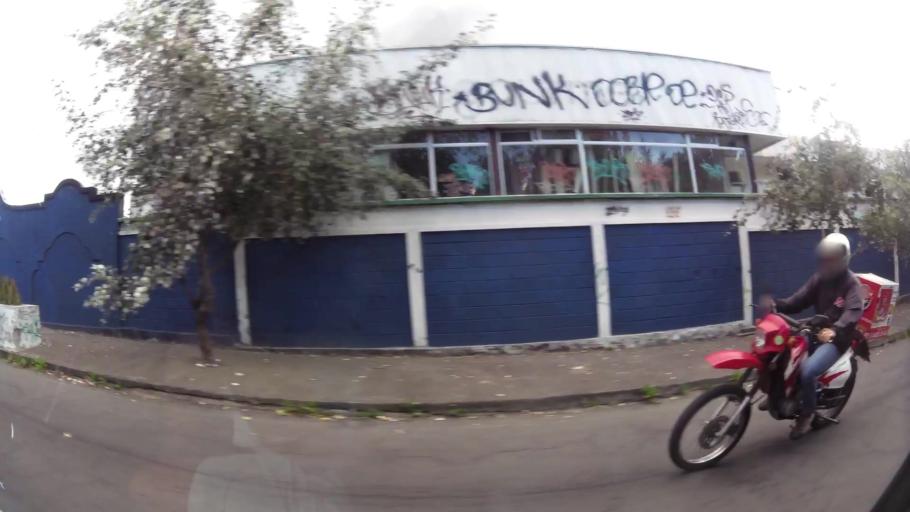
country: EC
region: Pichincha
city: Quito
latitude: -0.1279
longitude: -78.4893
